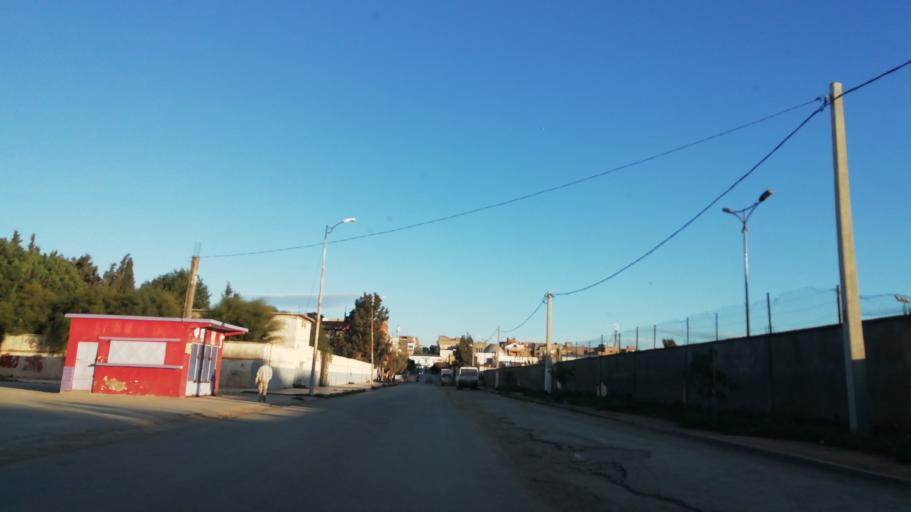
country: DZ
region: Oran
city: Sidi ech Chahmi
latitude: 35.6931
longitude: -0.5057
